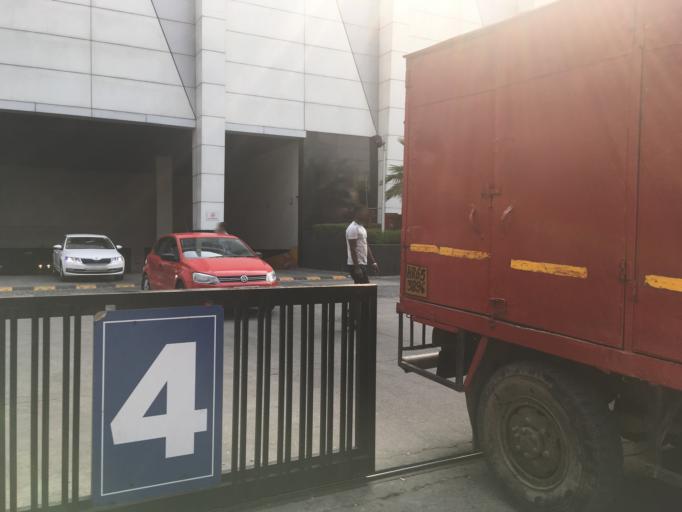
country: IN
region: Chandigarh
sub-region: Chandigarh
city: Chandigarh
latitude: 30.7061
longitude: 76.8017
